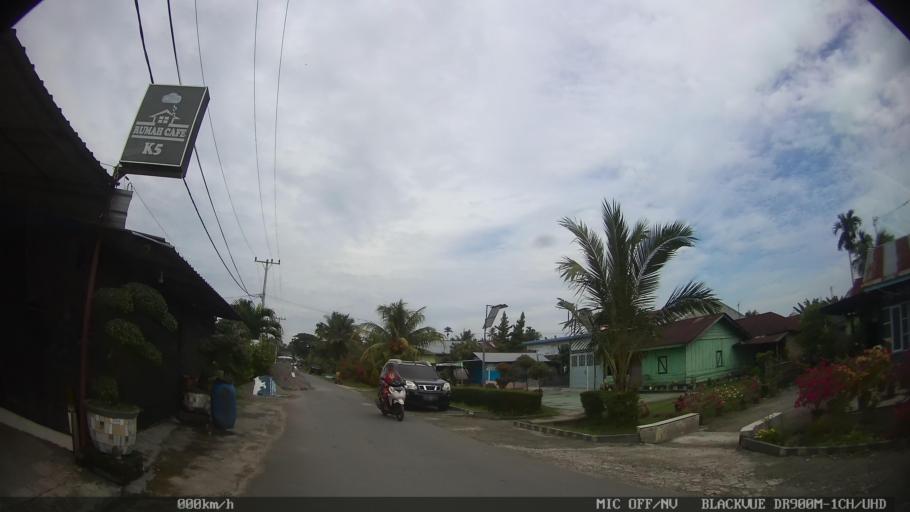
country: ID
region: North Sumatra
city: Sunggal
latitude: 3.6621
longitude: 98.5946
